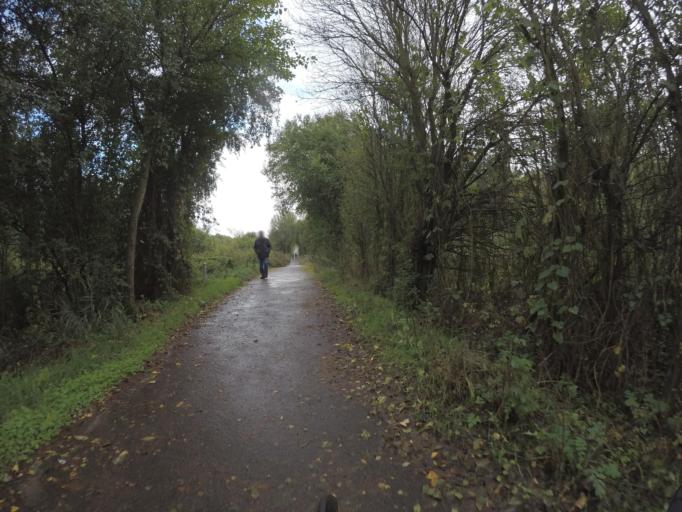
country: DE
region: Berlin
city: Lubars
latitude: 52.6237
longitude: 13.3691
